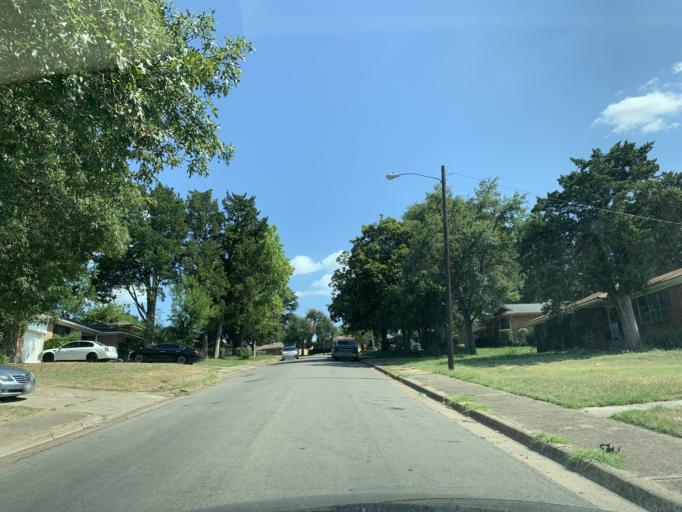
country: US
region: Texas
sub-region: Dallas County
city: Hutchins
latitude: 32.6785
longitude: -96.8036
